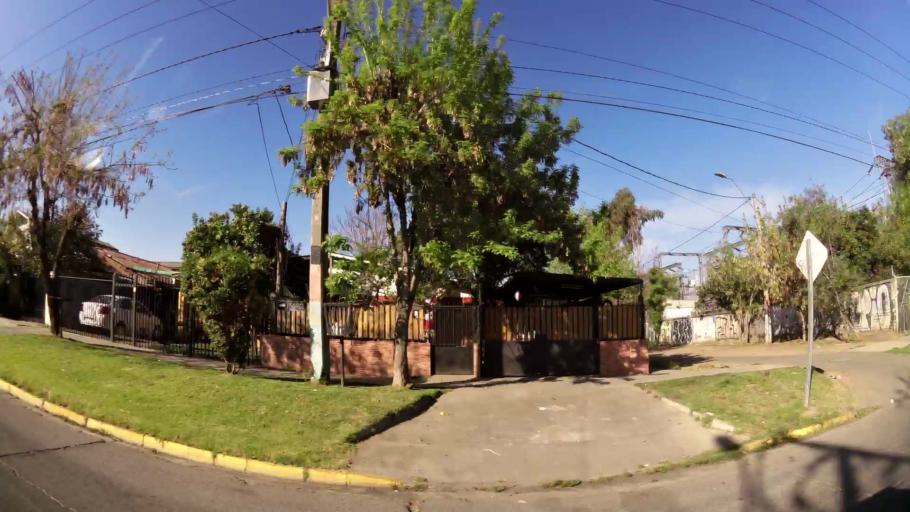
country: CL
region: Santiago Metropolitan
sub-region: Provincia de Santiago
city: Villa Presidente Frei, Nunoa, Santiago, Chile
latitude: -33.4619
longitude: -70.5644
